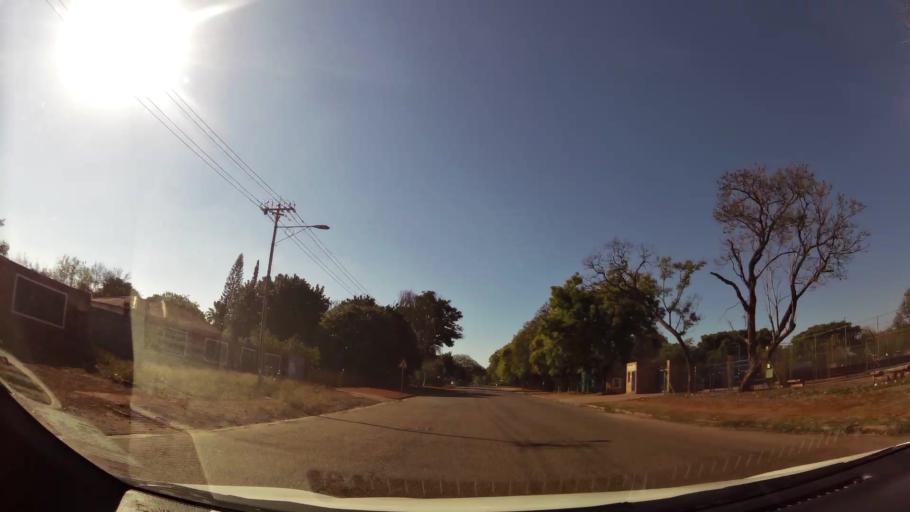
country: ZA
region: Limpopo
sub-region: Waterberg District Municipality
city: Mokopane
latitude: -24.1854
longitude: 29.0033
